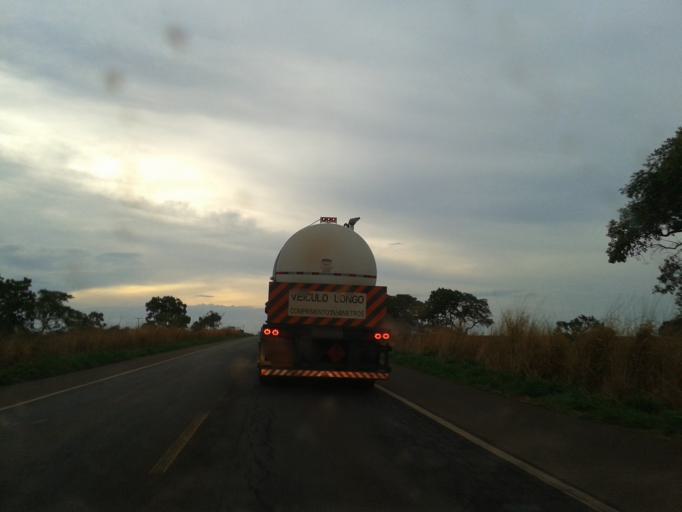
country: BR
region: Goias
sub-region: Santa Helena De Goias
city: Santa Helena de Goias
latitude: -17.9375
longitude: -50.5354
